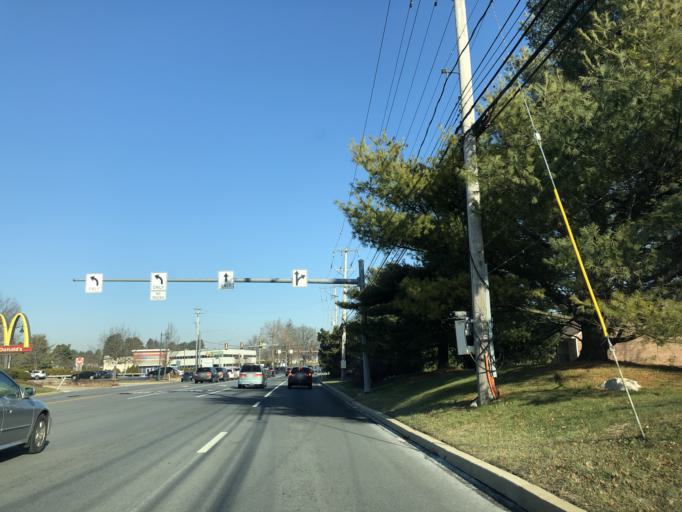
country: US
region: Pennsylvania
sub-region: Chester County
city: Exton
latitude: 40.0492
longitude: -75.6618
